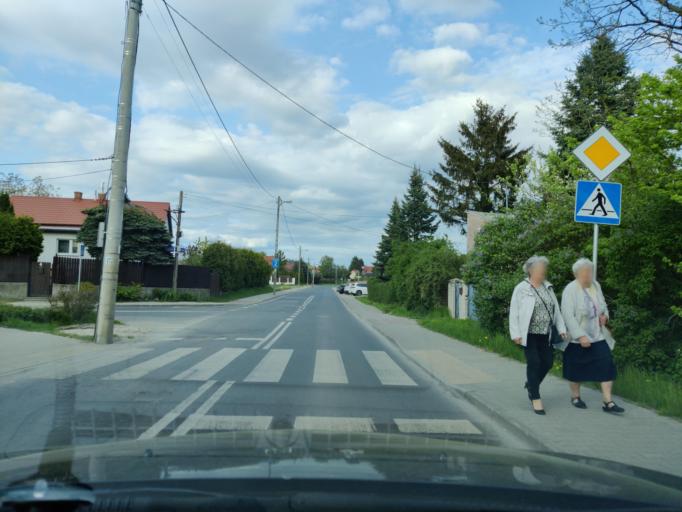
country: PL
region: Masovian Voivodeship
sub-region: Warszawa
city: Kabaty
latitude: 52.1282
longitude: 21.1046
